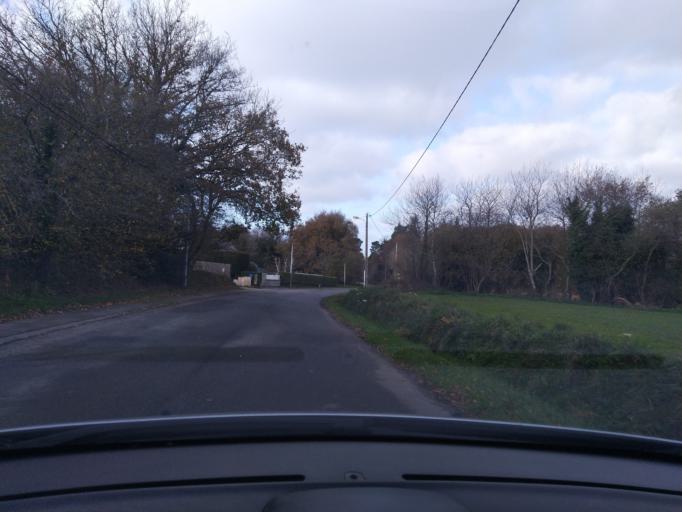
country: FR
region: Brittany
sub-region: Departement du Finistere
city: Plouigneau
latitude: 48.5723
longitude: -3.7054
